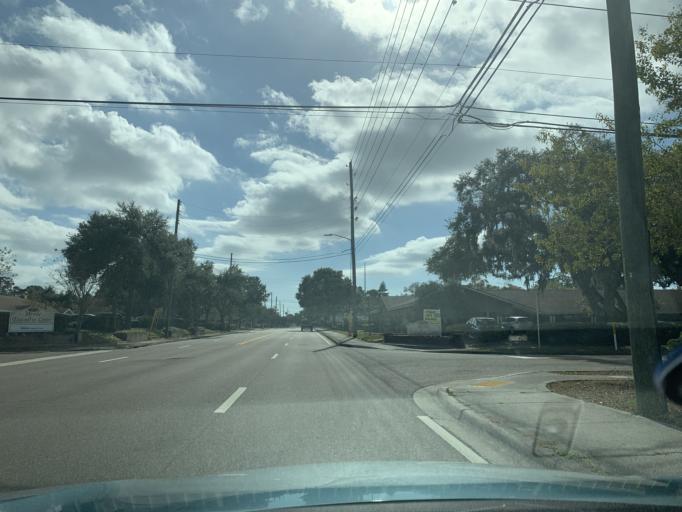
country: US
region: Florida
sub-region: Pinellas County
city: Clearwater
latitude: 27.9530
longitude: -82.7959
